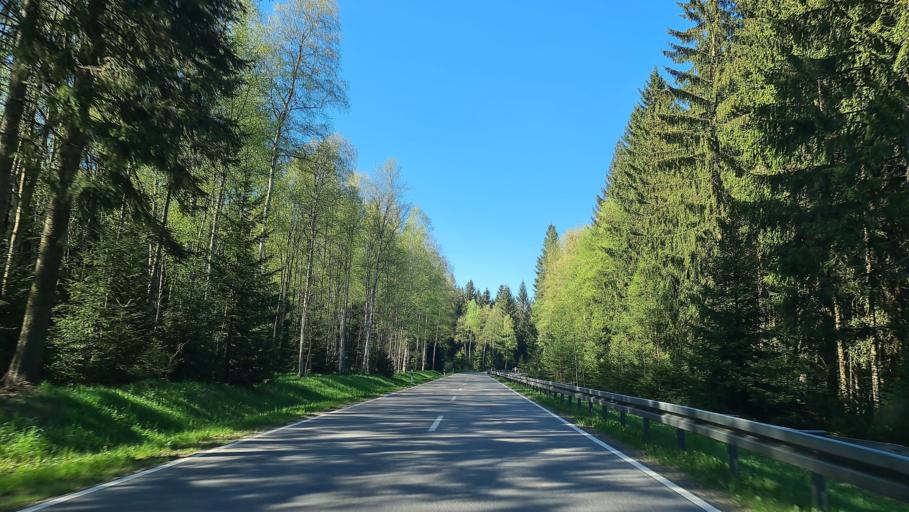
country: DE
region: Saxony
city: Hammerbrucke
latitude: 50.4292
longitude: 12.4013
